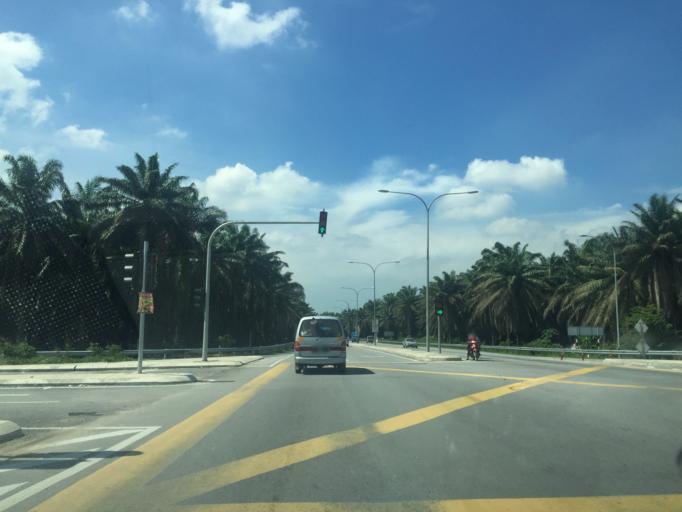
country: MY
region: Penang
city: Tasek Glugor
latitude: 5.5125
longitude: 100.5331
